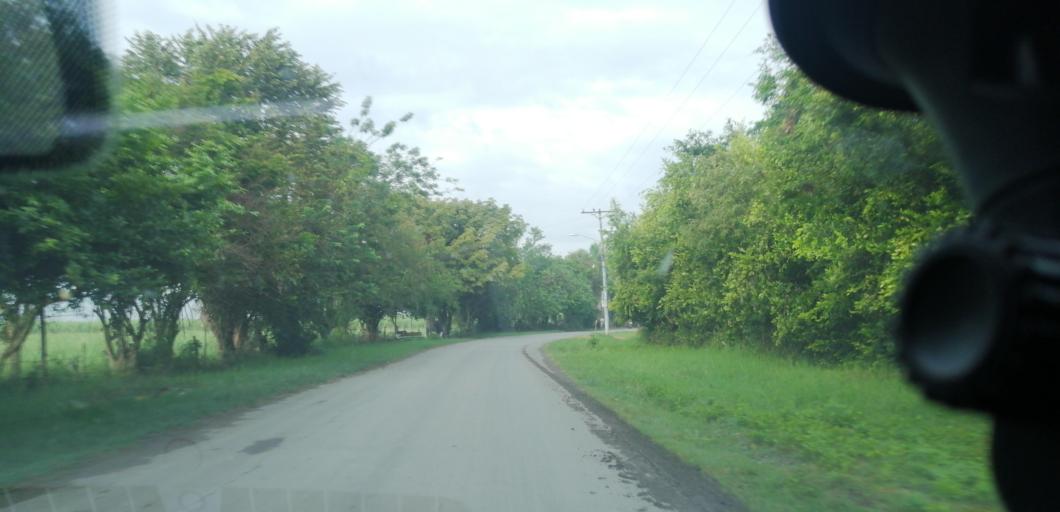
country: CO
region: Valle del Cauca
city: Palmira
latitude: 3.5367
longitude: -76.3555
